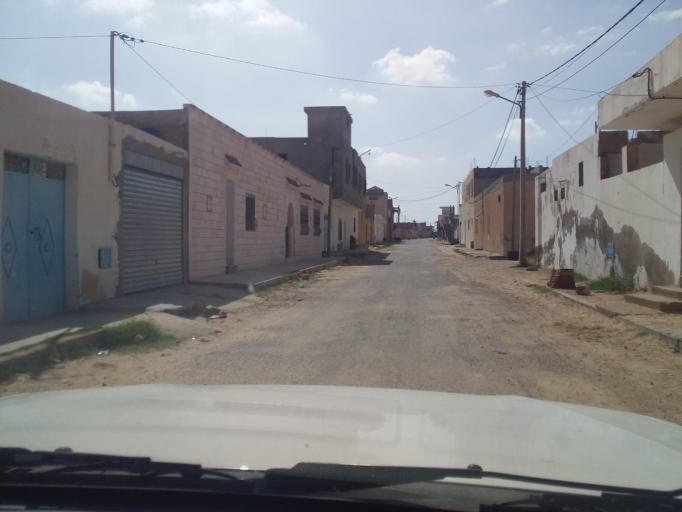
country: TN
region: Madanin
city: Medenine
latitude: 33.5834
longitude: 10.3227
